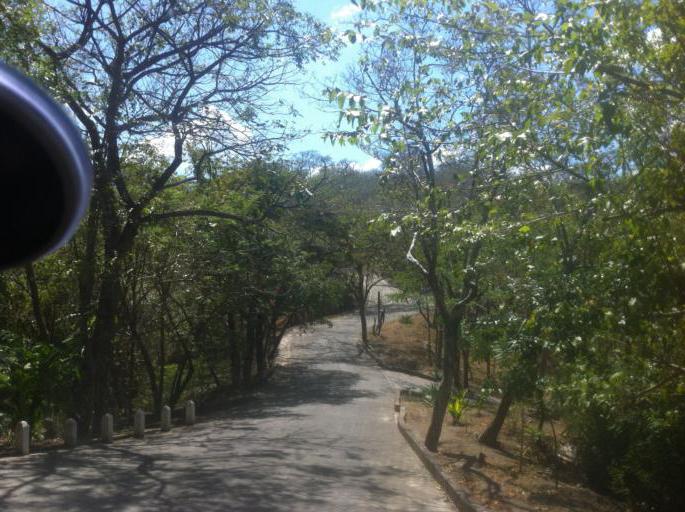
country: NI
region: Rivas
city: Tola
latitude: 11.3809
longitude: -86.0298
